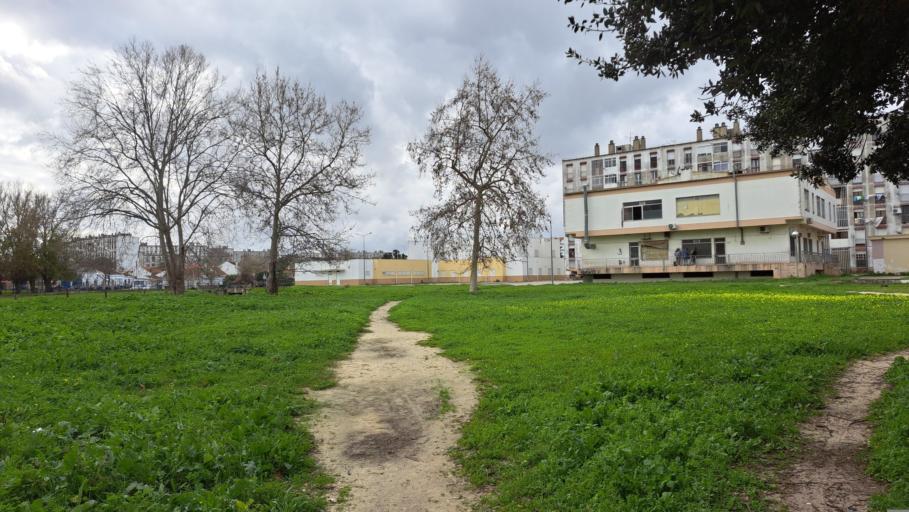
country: PT
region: Setubal
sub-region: Moita
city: Alhos Vedros
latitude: 38.6508
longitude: -9.0370
